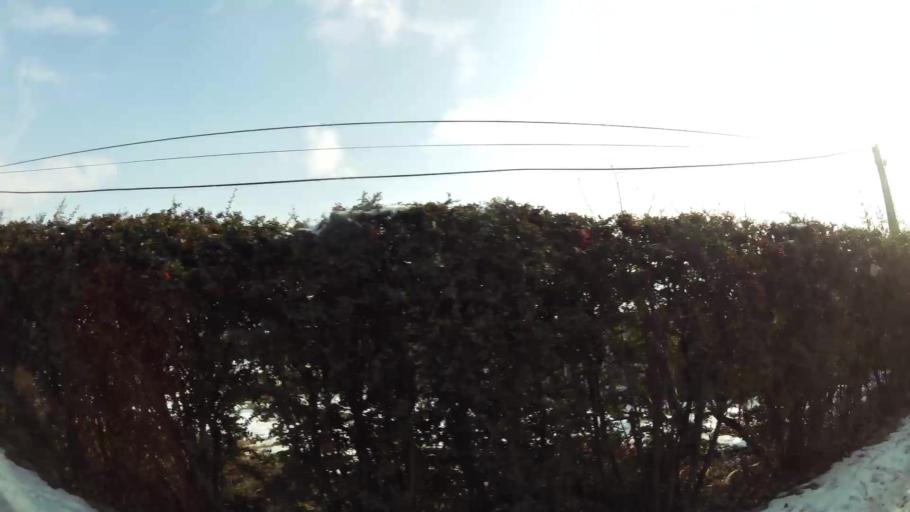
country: MK
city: Creshevo
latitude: 42.0126
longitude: 21.5007
